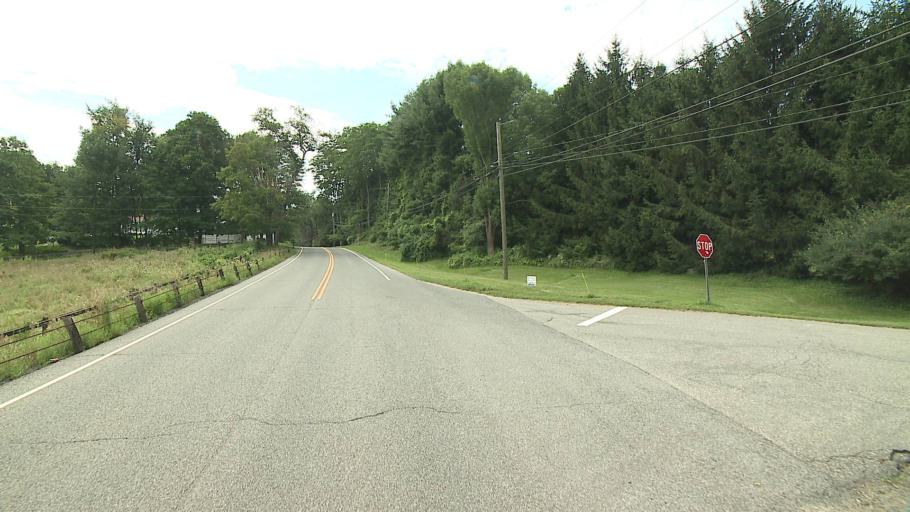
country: US
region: Connecticut
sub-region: Fairfield County
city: Sherman
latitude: 41.6254
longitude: -73.5079
